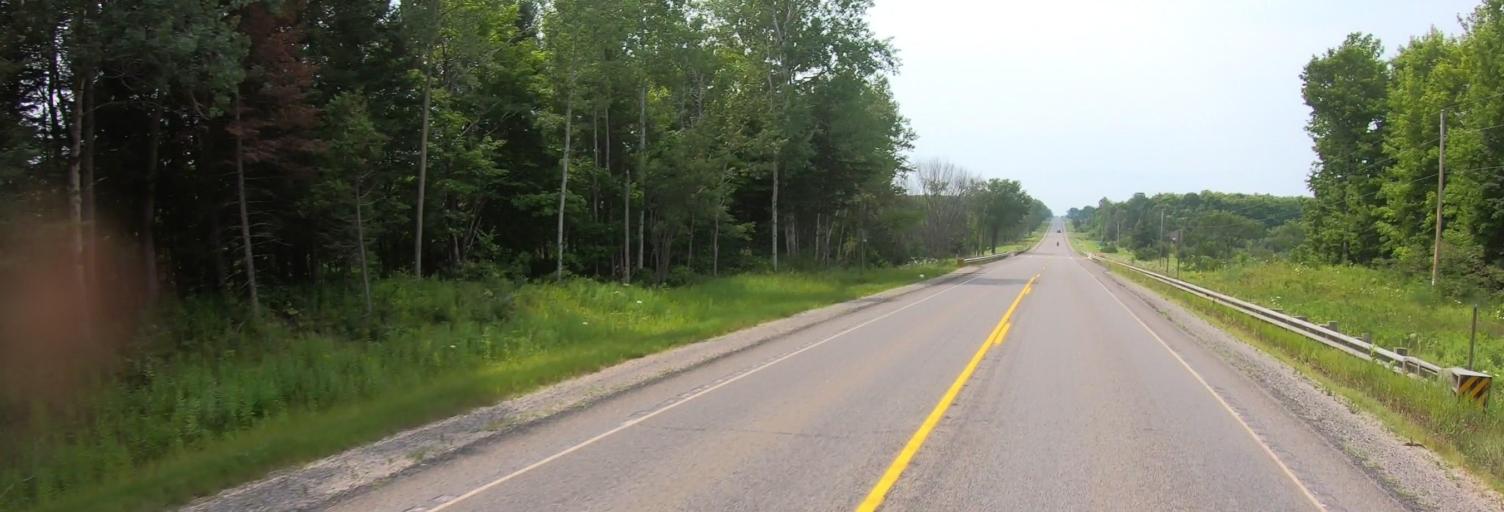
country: US
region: Michigan
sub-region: Alger County
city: Munising
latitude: 46.3329
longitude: -86.8774
